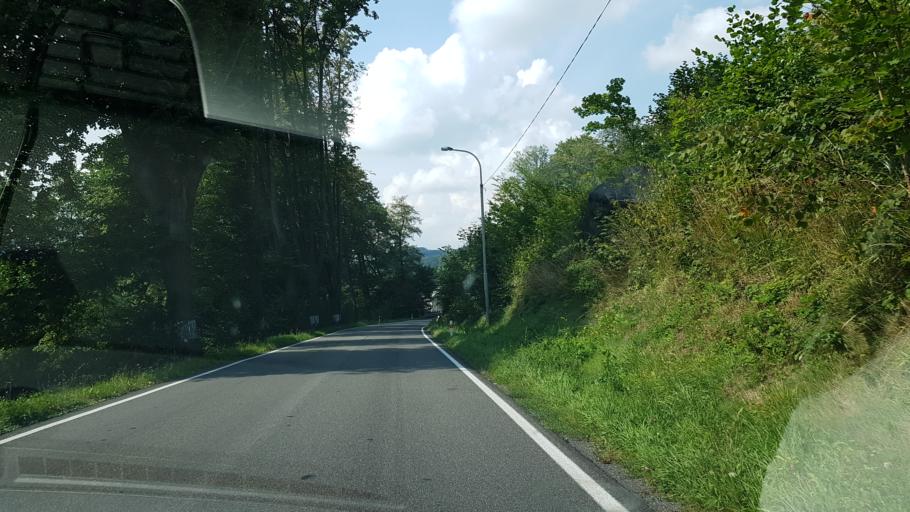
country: CZ
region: Olomoucky
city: Pisecna
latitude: 50.2713
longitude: 17.2565
